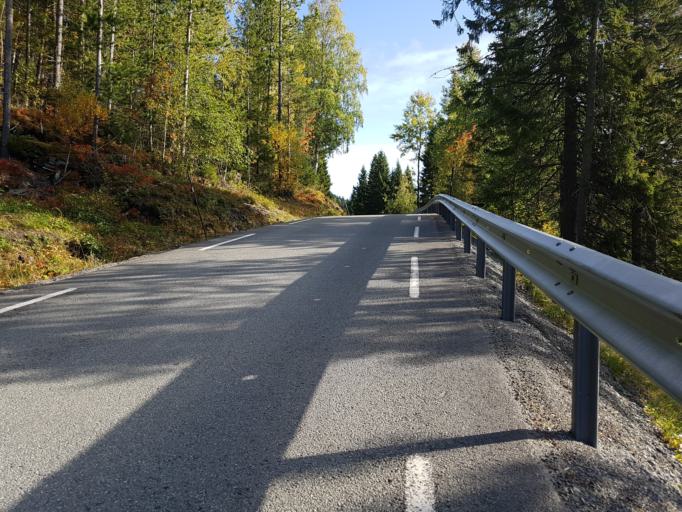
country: NO
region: Sor-Trondelag
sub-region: Malvik
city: Malvik
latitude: 63.3584
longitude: 10.6349
